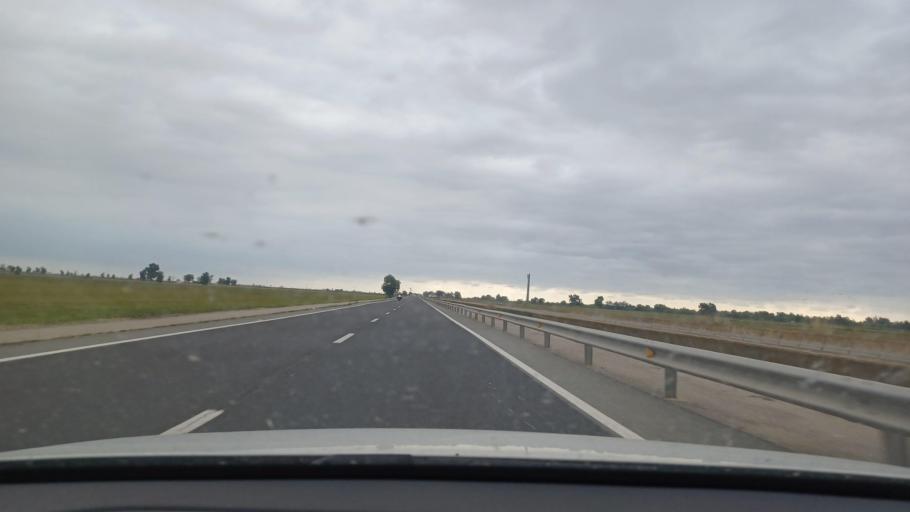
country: ES
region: Catalonia
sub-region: Provincia de Tarragona
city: Amposta
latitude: 40.7144
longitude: 0.6251
